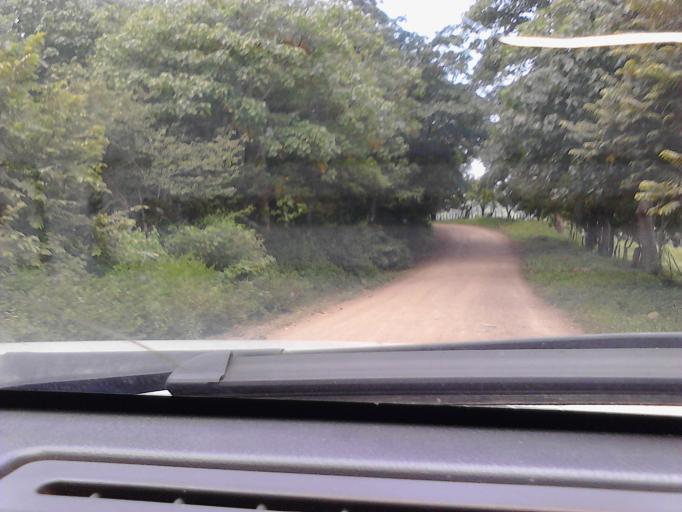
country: NI
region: Matagalpa
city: Terrabona
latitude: 12.7055
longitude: -85.9495
